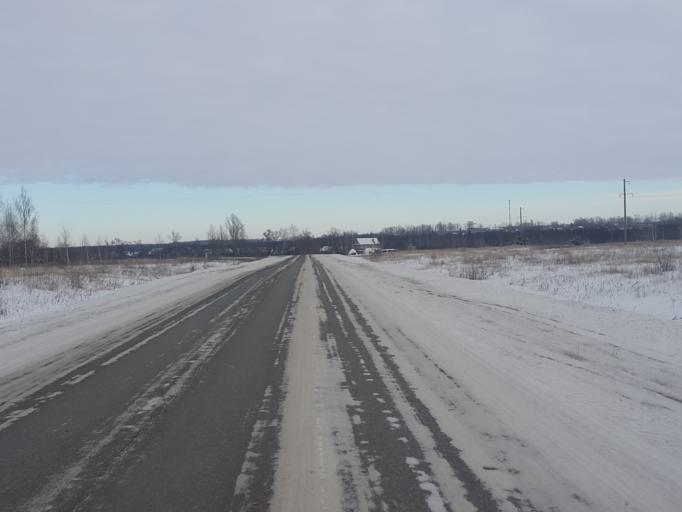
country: RU
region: Tambov
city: Platonovka
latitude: 52.8700
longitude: 41.8643
